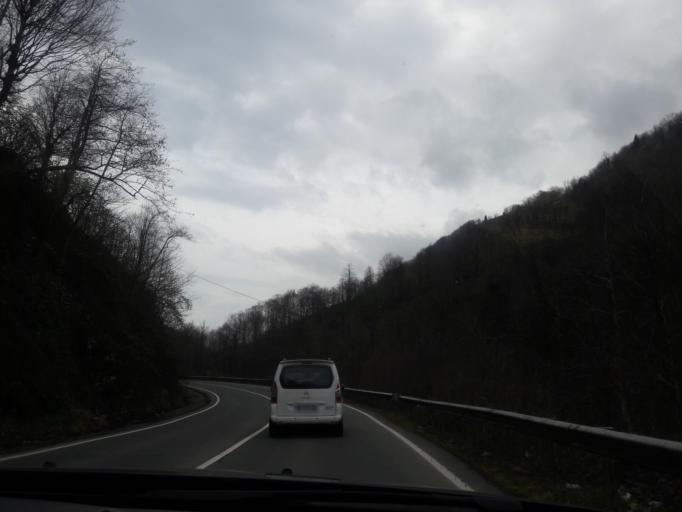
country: TR
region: Trabzon
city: Salpazari
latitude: 40.9792
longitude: 39.1974
